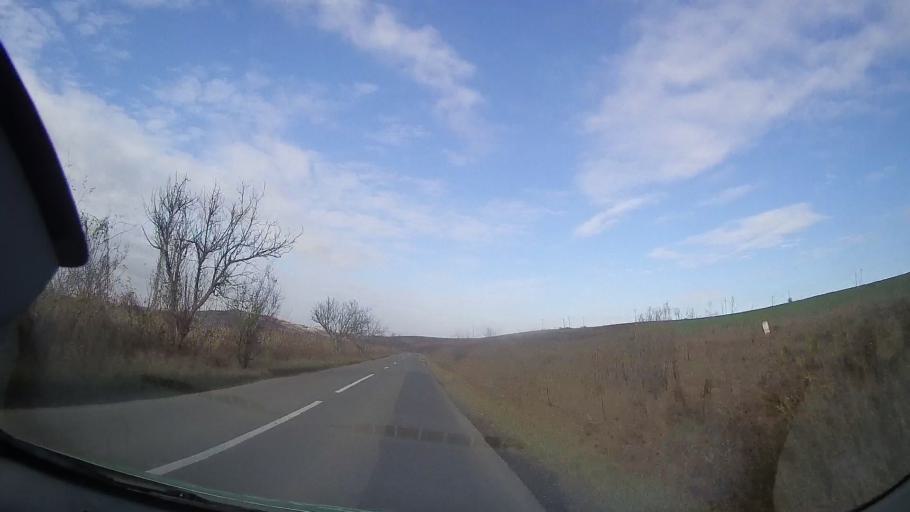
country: RO
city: Barza
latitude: 46.5629
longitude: 24.0980
